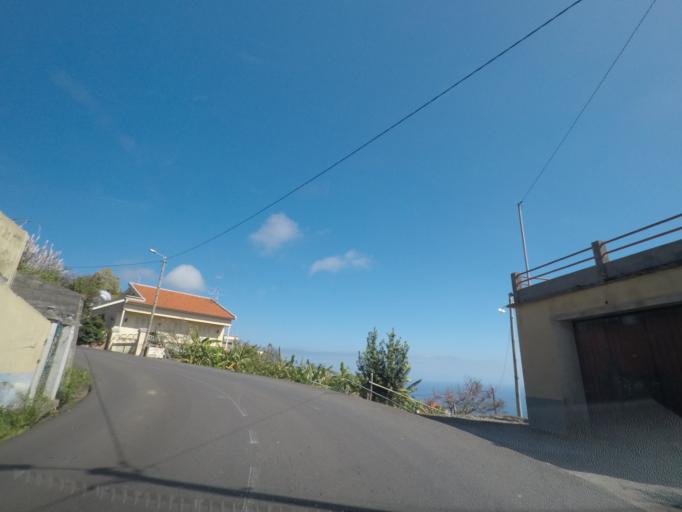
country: PT
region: Madeira
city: Ponta do Sol
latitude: 32.6960
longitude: -17.1003
